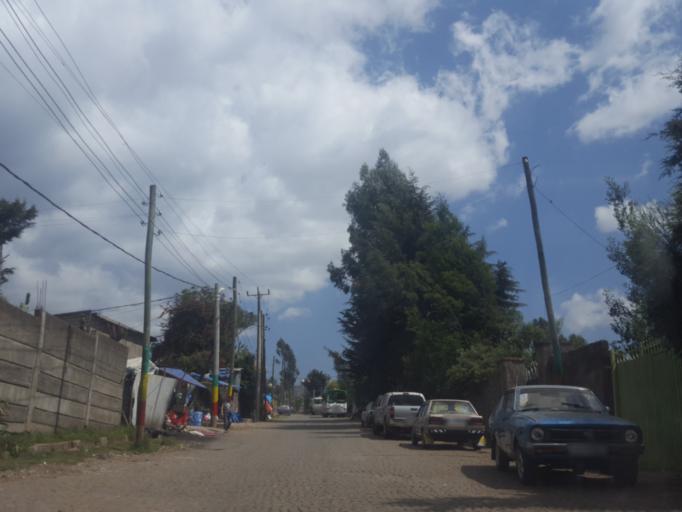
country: ET
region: Adis Abeba
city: Addis Ababa
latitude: 9.0547
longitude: 38.7266
